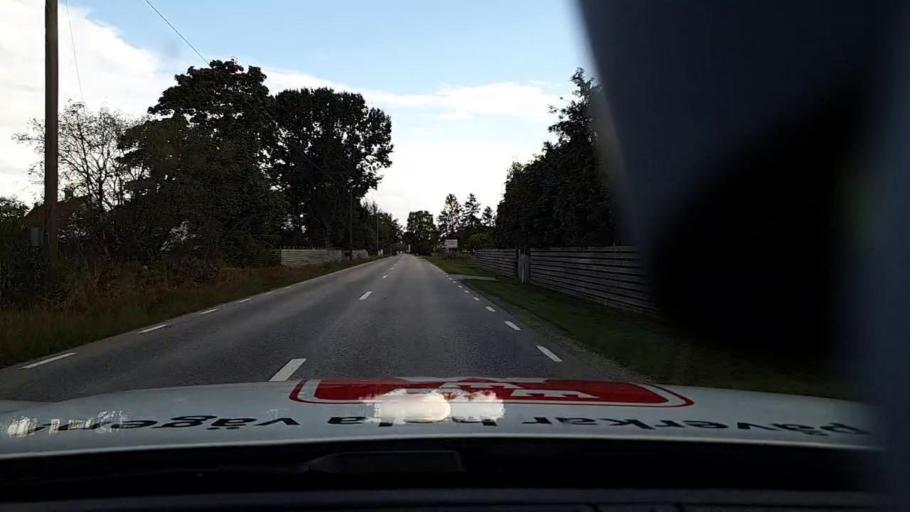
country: SE
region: Blekinge
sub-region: Solvesborgs Kommun
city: Soelvesborg
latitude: 56.0195
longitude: 14.7166
